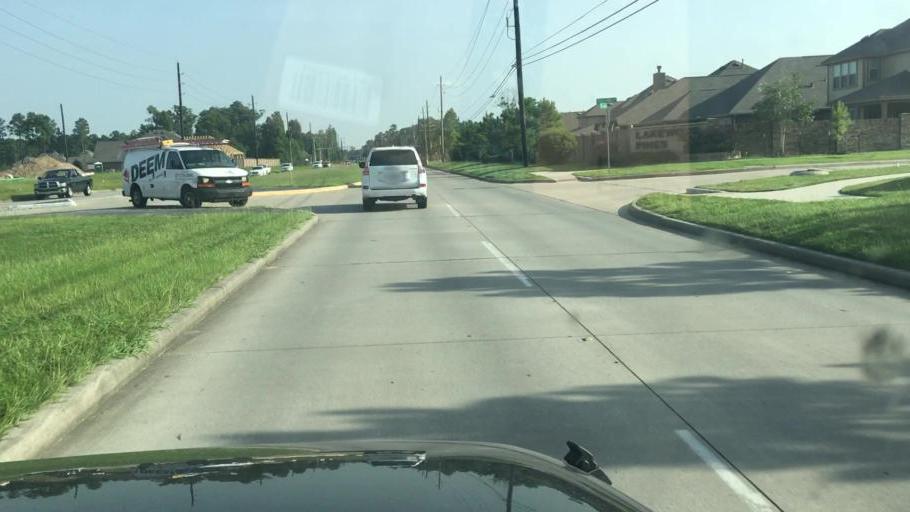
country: US
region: Texas
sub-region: Harris County
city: Atascocita
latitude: 29.9473
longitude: -95.1751
